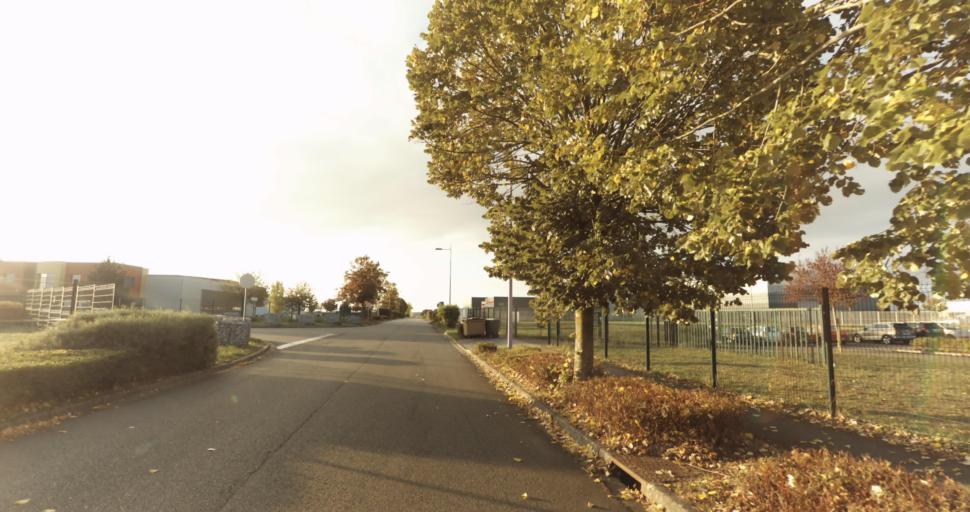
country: FR
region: Centre
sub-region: Departement d'Eure-et-Loir
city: Vernouillet
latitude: 48.7112
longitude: 1.3713
